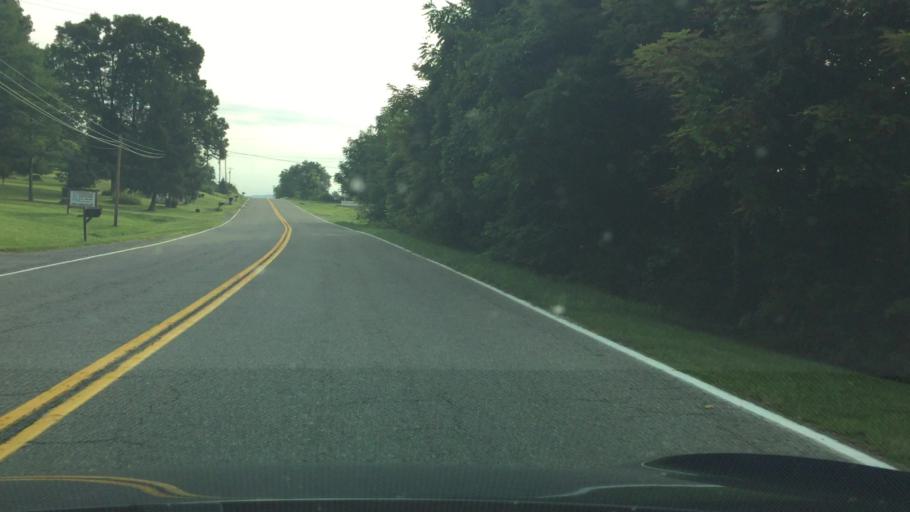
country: US
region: Virginia
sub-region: Pulaski County
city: Pulaski
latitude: 36.9590
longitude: -80.8596
